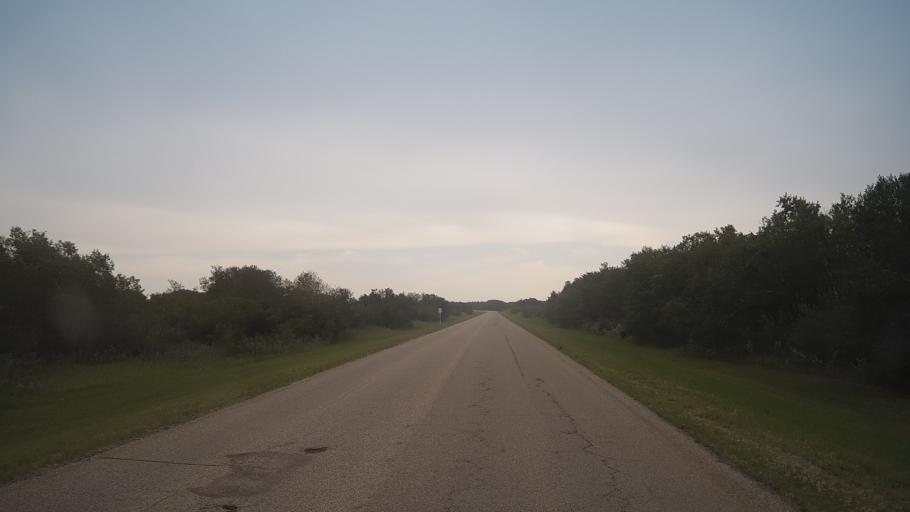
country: CA
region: Saskatchewan
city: Saskatoon
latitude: 51.8454
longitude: -106.5478
